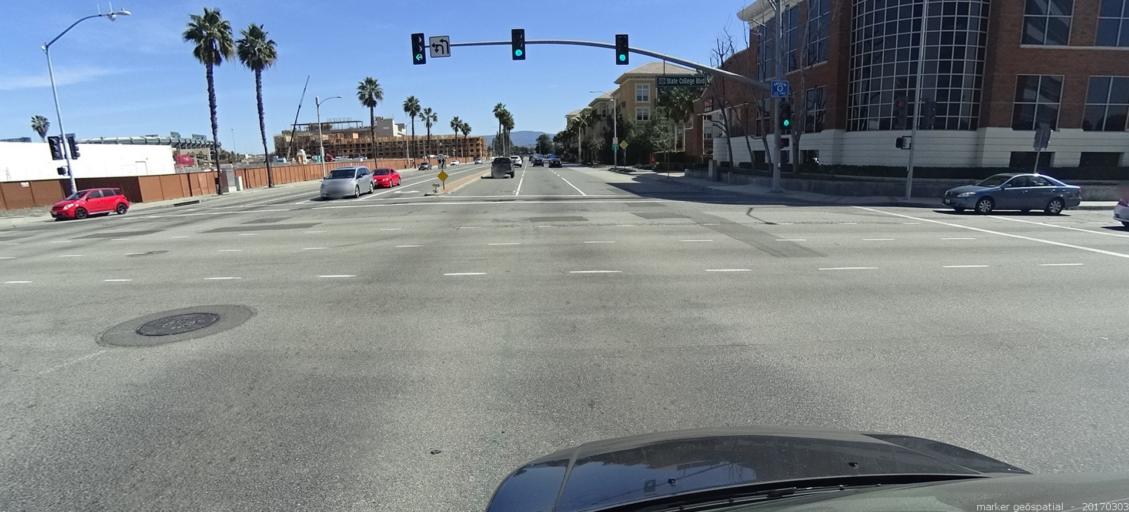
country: US
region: California
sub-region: Orange County
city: Orange
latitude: 33.7961
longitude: -117.8892
